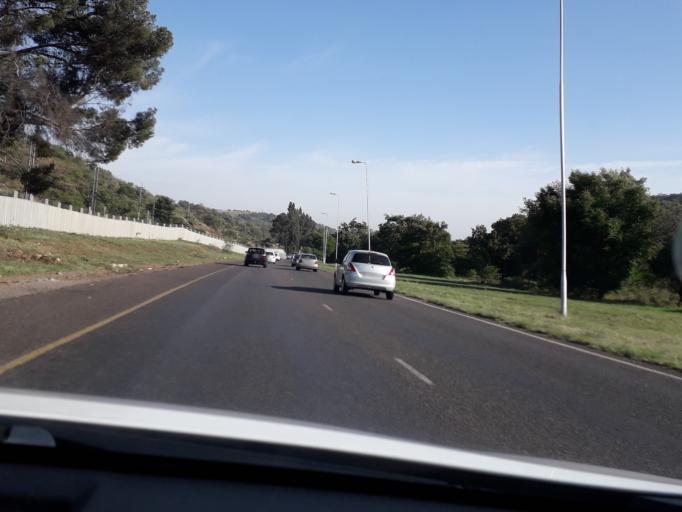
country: ZA
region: Gauteng
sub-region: City of Tshwane Metropolitan Municipality
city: Centurion
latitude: -25.8054
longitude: 28.1985
